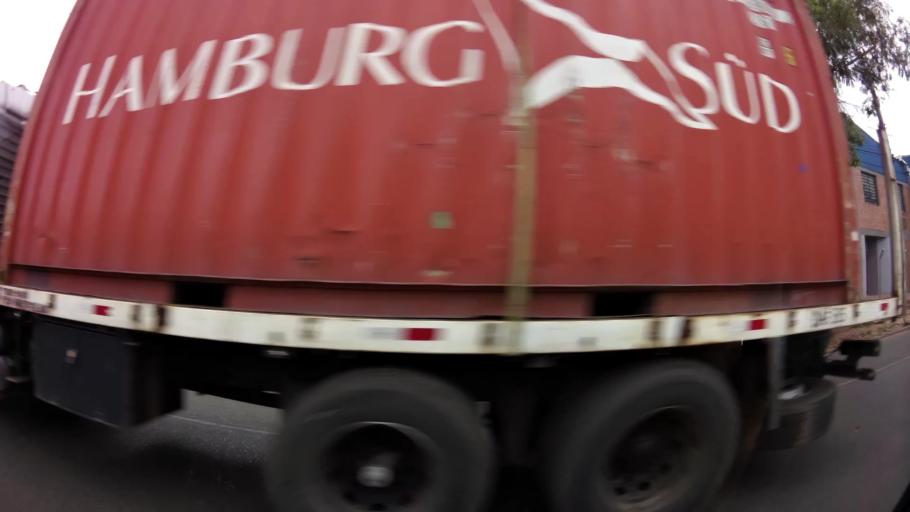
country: PY
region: Central
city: San Lorenzo
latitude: -25.2903
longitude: -57.5009
